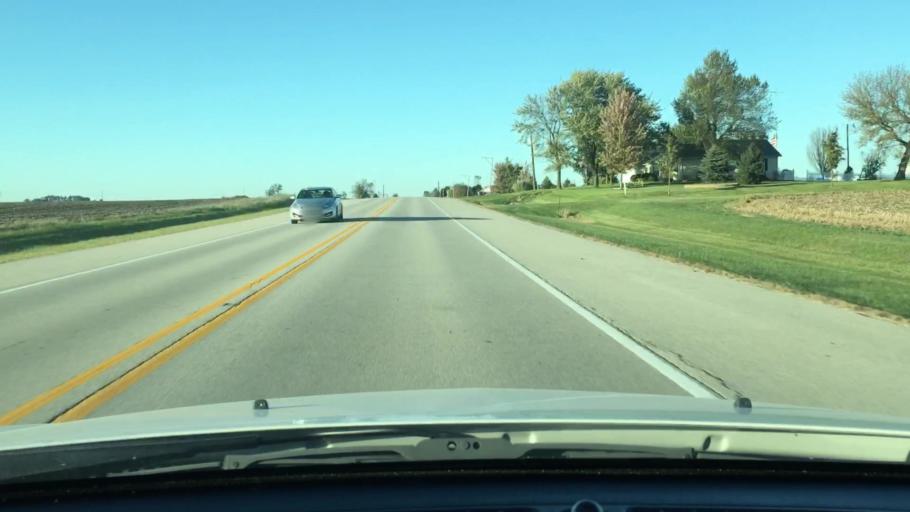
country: US
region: Illinois
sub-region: DeKalb County
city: Waterman
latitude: 41.8158
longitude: -88.7539
